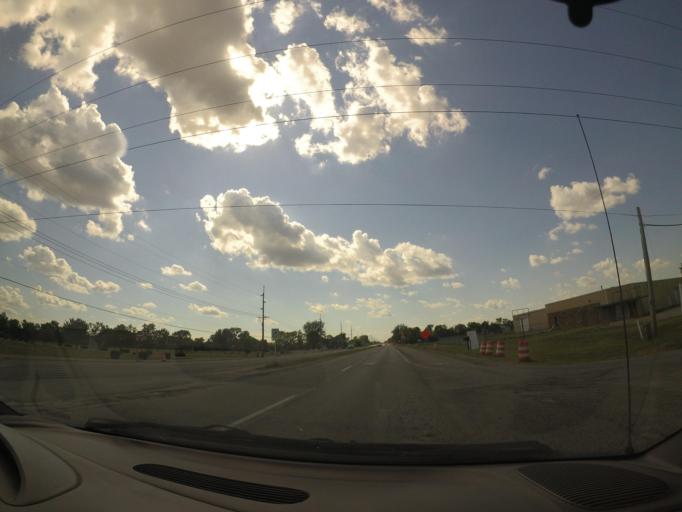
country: US
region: Ohio
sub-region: Sandusky County
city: Clyde
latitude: 41.3219
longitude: -83.0183
